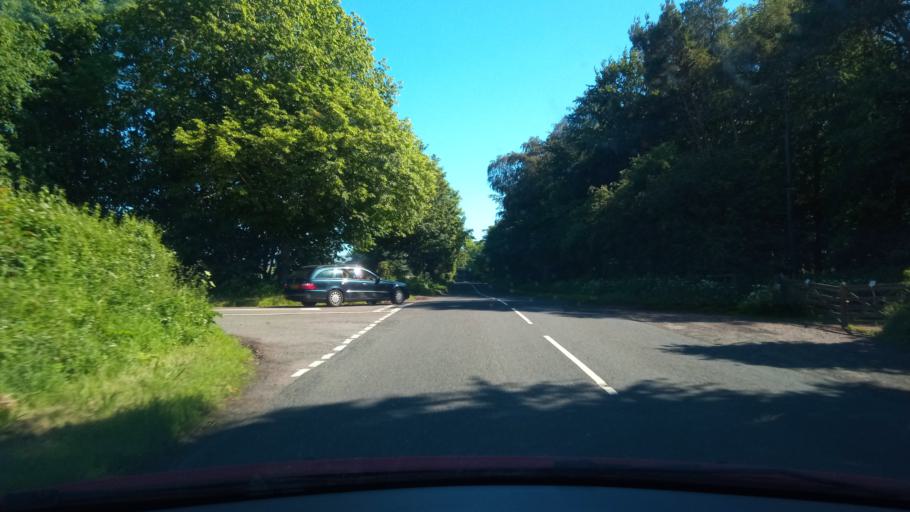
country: GB
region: Scotland
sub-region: East Lothian
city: East Linton
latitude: 56.0124
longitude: -2.6312
